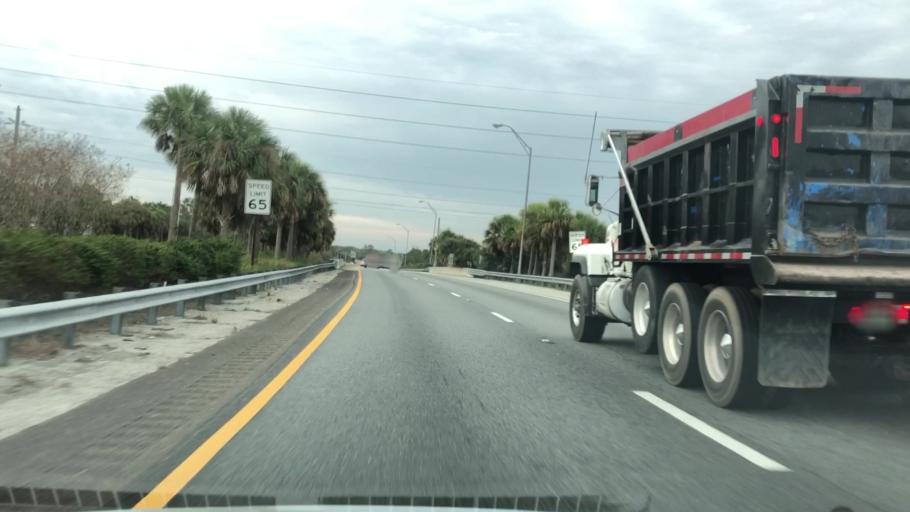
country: US
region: Florida
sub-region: Seminole County
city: Goldenrod
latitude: 28.6197
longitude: -81.2595
